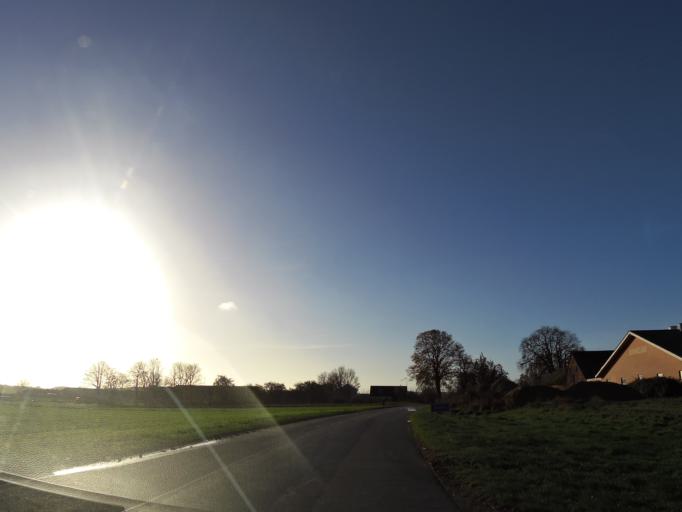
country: DK
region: Central Jutland
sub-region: Odder Kommune
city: Odder
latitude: 55.9398
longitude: 10.2360
